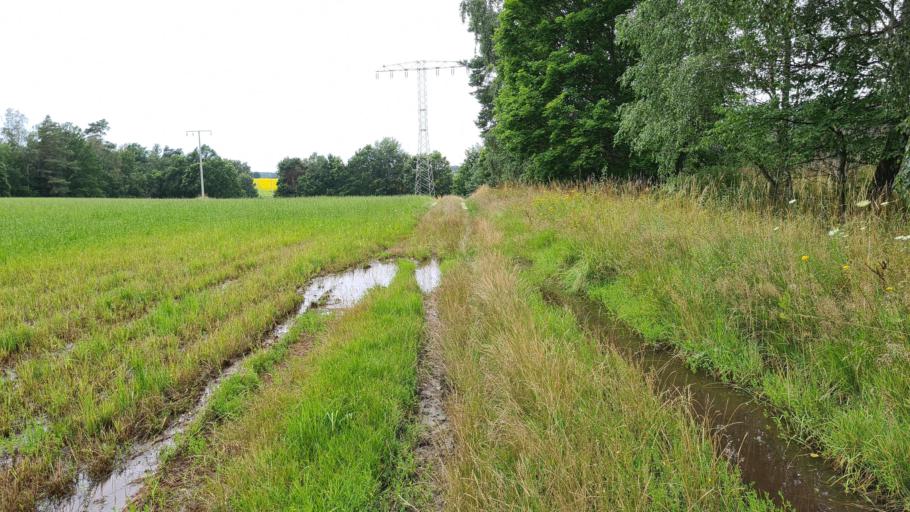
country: DE
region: Brandenburg
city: Crinitz
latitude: 51.7357
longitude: 13.7402
